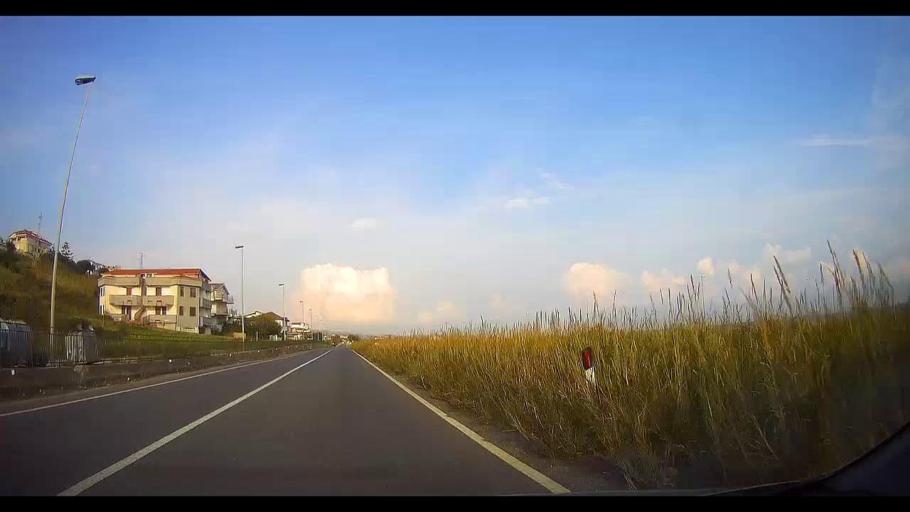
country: IT
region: Calabria
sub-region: Provincia di Cosenza
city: Cariati
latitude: 39.5282
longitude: 16.8861
